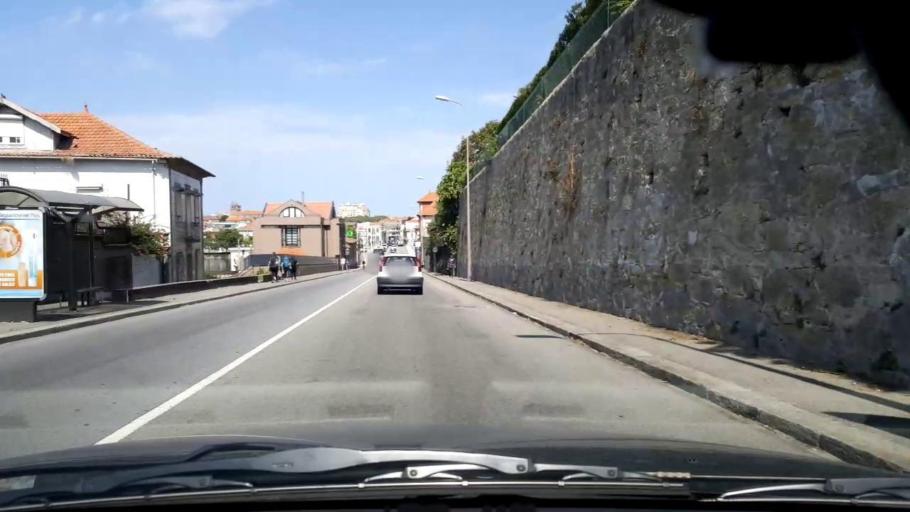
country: PT
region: Porto
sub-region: Vila do Conde
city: Vila do Conde
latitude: 41.3492
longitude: -8.7384
